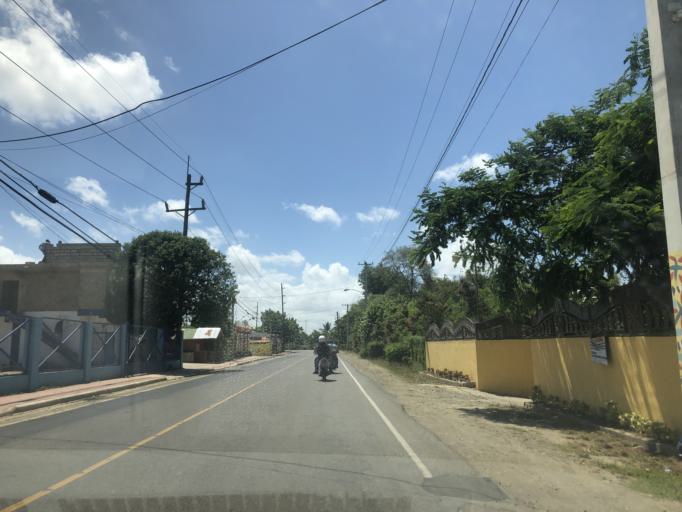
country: DO
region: Santiago
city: La Canela
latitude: 19.4507
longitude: -70.7745
